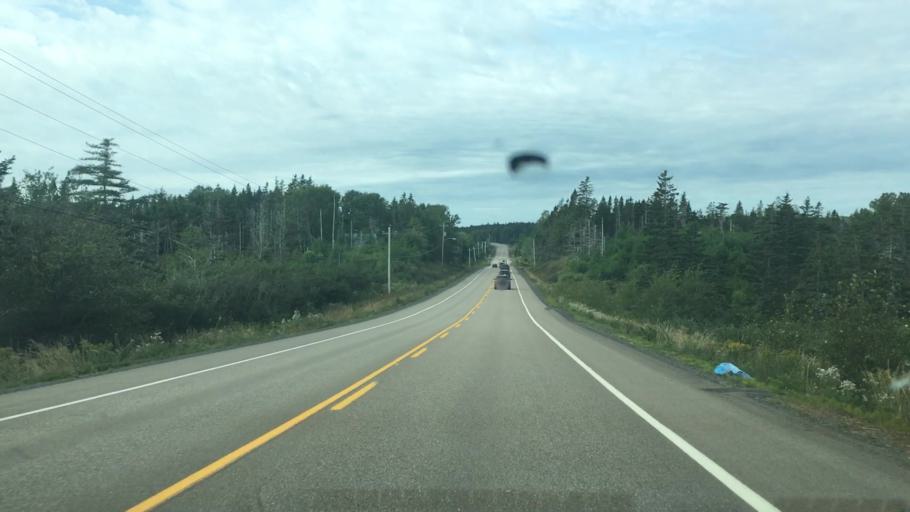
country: CA
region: Nova Scotia
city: Princeville
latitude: 45.6938
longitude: -60.7400
